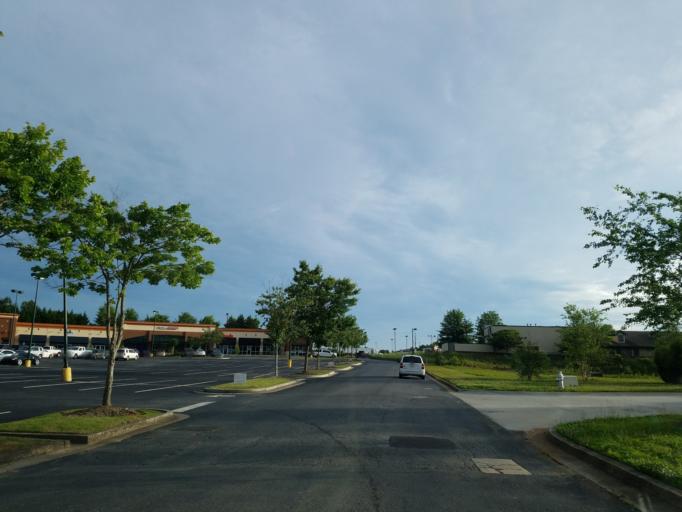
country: US
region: Georgia
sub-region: Dawson County
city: Dawsonville
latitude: 34.3648
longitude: -84.0330
